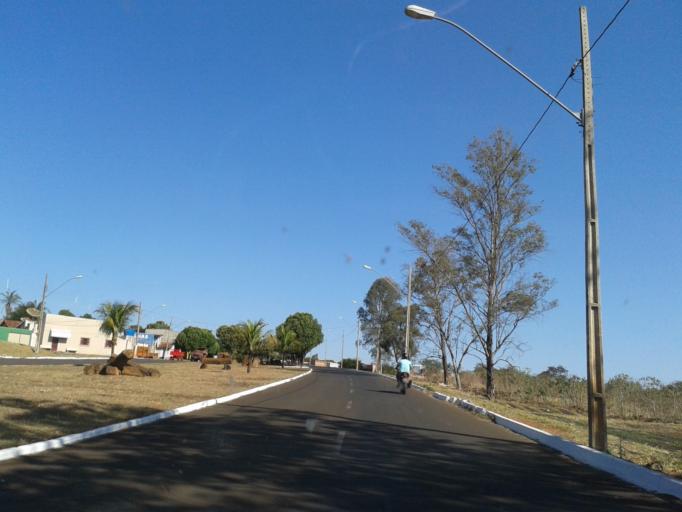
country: BR
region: Minas Gerais
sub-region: Santa Vitoria
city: Santa Vitoria
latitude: -18.8494
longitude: -50.1317
